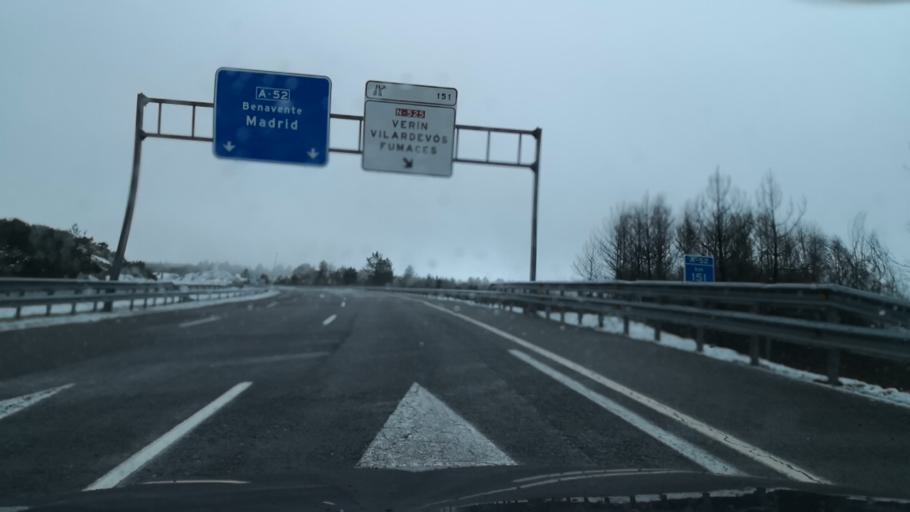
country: ES
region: Galicia
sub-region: Provincia de Ourense
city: Rios
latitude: 41.9498
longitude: -7.3508
